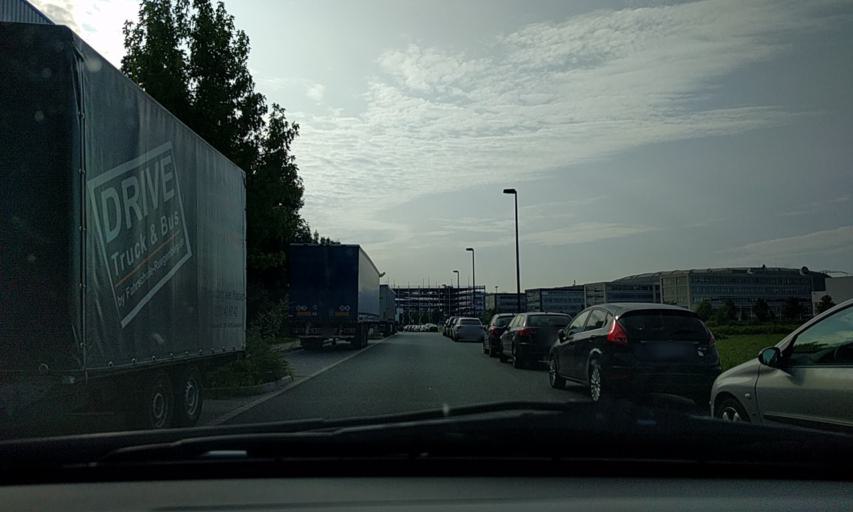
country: DE
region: North Rhine-Westphalia
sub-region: Regierungsbezirk Dusseldorf
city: Ratingen
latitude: 51.2766
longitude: 6.8091
